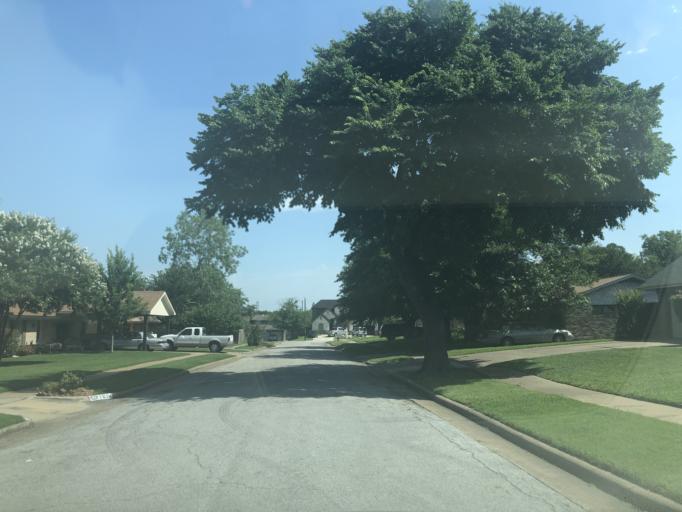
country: US
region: Texas
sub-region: Dallas County
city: Grand Prairie
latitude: 32.7233
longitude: -97.0034
